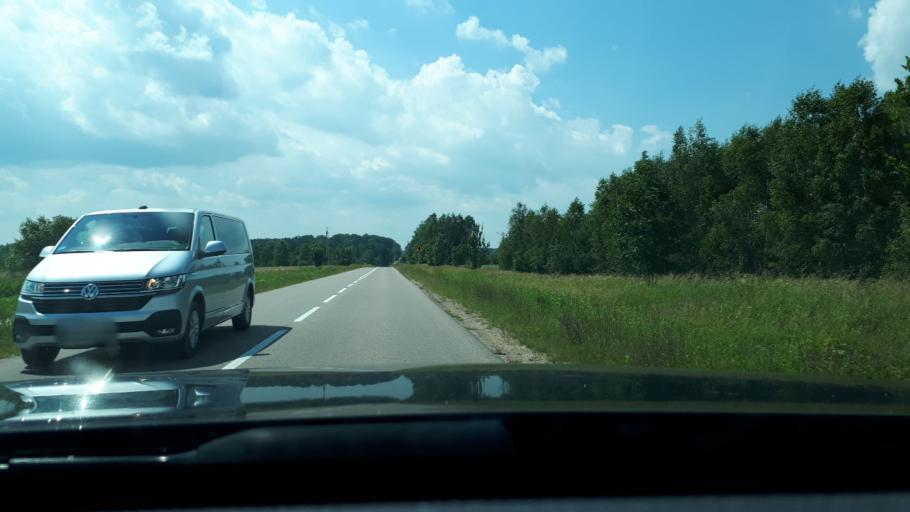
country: PL
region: Podlasie
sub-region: Powiat bialostocki
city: Choroszcz
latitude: 53.1255
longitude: 22.9684
